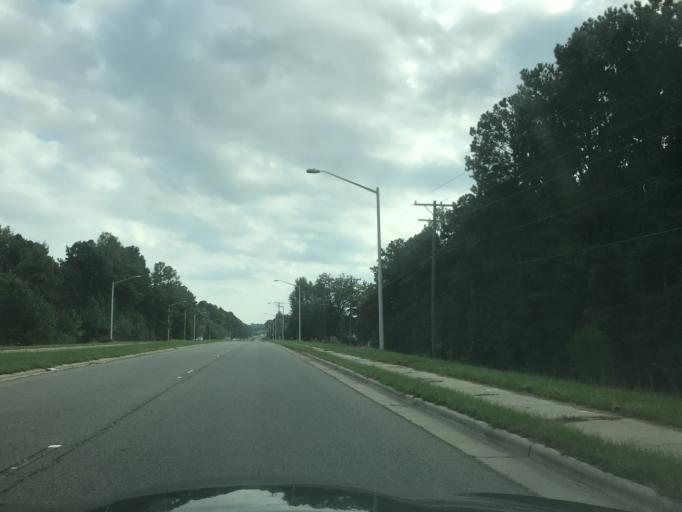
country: US
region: North Carolina
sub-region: Durham County
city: Durham
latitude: 35.9263
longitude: -78.8895
